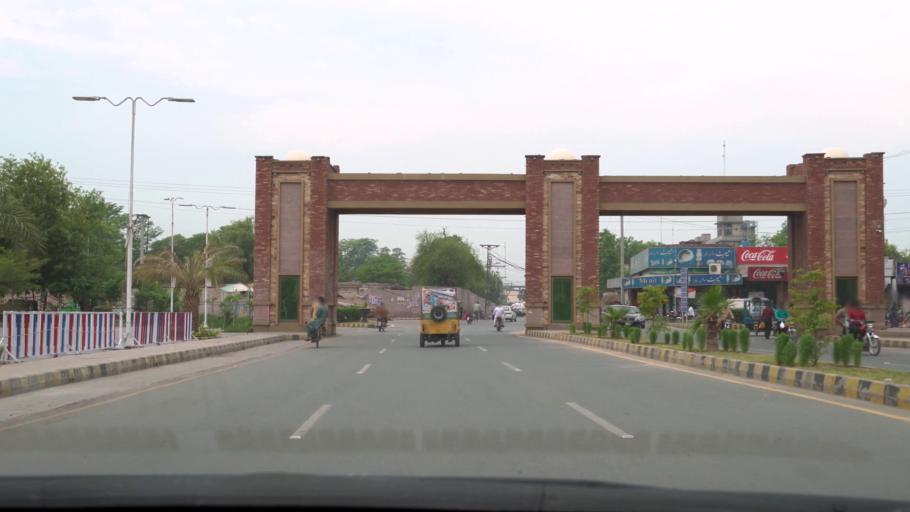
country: PK
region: Punjab
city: Faisalabad
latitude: 31.4314
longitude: 73.0825
